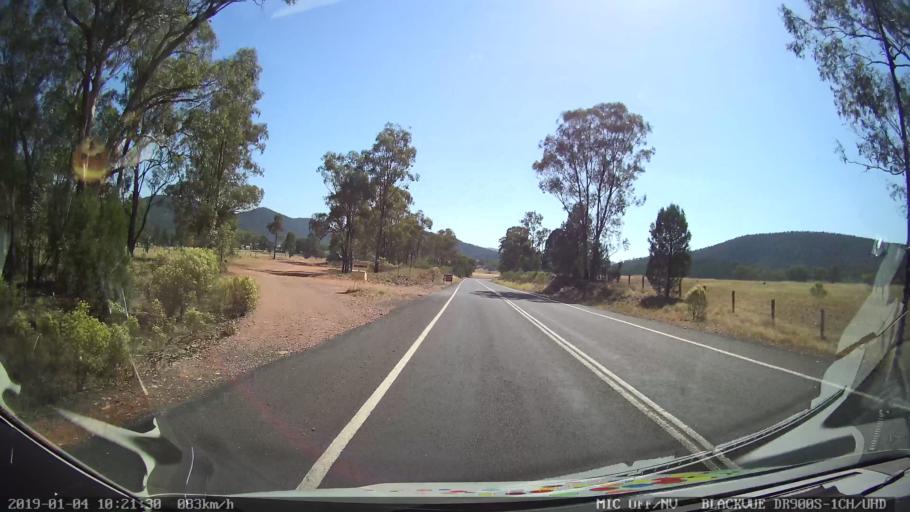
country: AU
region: New South Wales
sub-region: Cabonne
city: Canowindra
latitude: -33.3724
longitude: 148.5113
